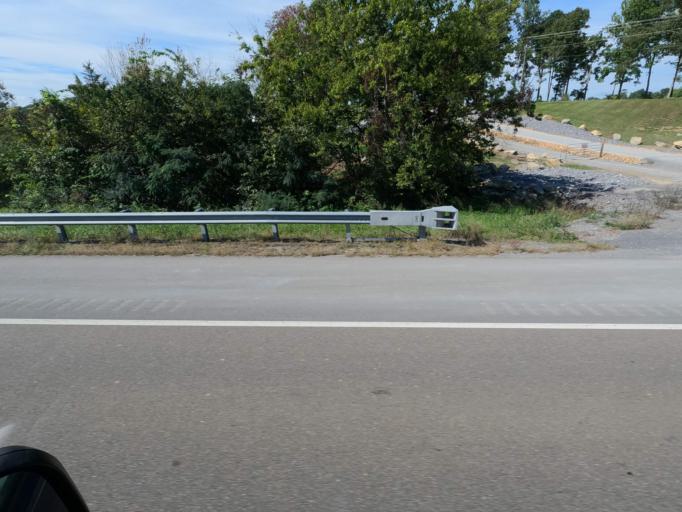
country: US
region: Tennessee
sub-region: Grainger County
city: Bean Station
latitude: 36.2860
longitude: -83.2800
